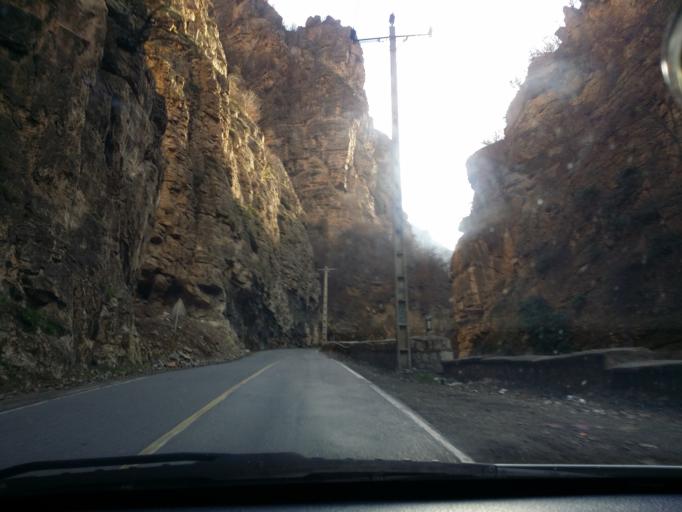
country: IR
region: Mazandaran
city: Chalus
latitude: 36.2709
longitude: 51.2463
